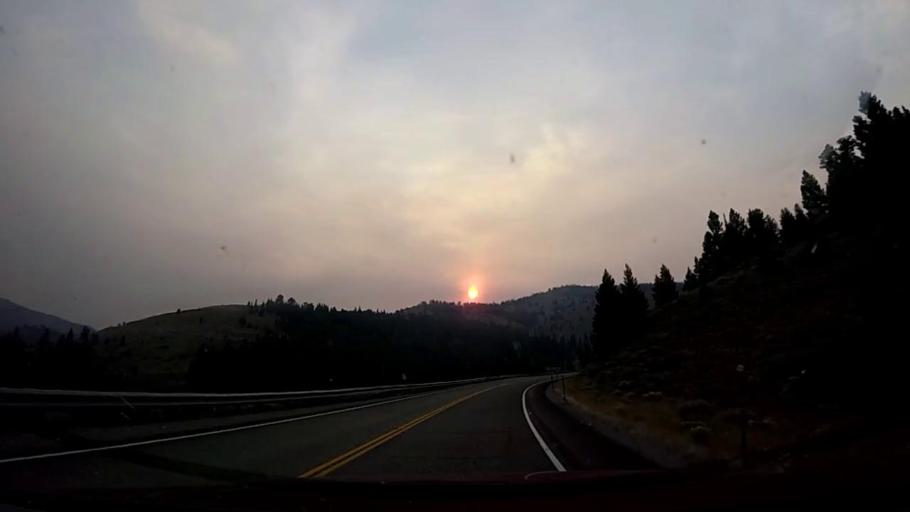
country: US
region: Idaho
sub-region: Blaine County
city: Ketchum
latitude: 43.8853
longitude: -114.6916
